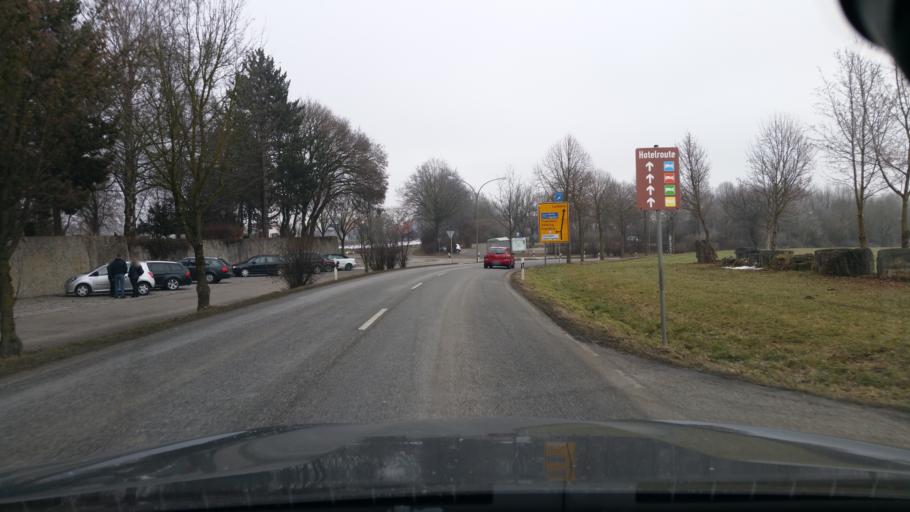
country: DE
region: Bavaria
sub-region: Lower Bavaria
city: Ergolding
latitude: 48.5626
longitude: 12.1299
